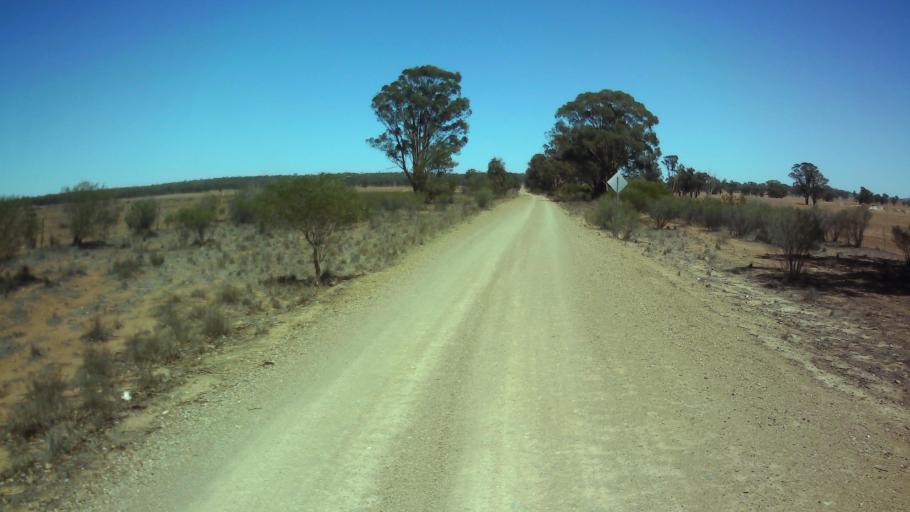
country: AU
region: New South Wales
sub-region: Forbes
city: Forbes
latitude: -33.6998
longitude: 147.8667
